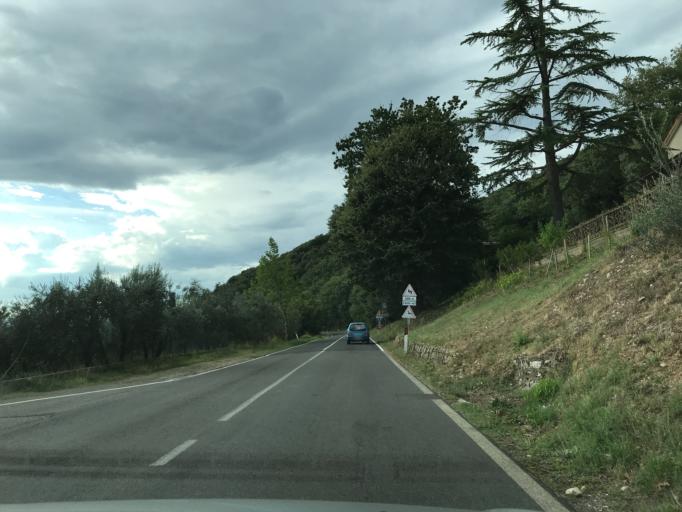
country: IT
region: Umbria
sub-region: Provincia di Terni
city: Guardea
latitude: 42.6307
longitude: 12.2960
